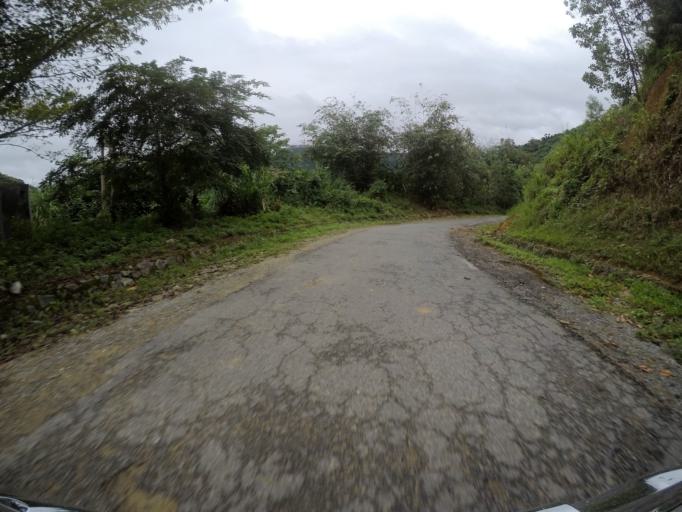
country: VN
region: Quang Nam
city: Prao
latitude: 15.6380
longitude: 107.5563
